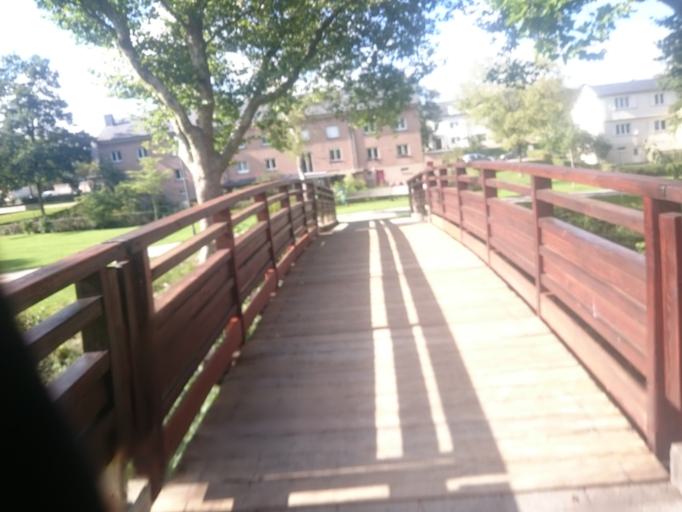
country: LU
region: Luxembourg
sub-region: Canton de Luxembourg
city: Luxembourg
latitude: 49.5898
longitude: 6.1048
